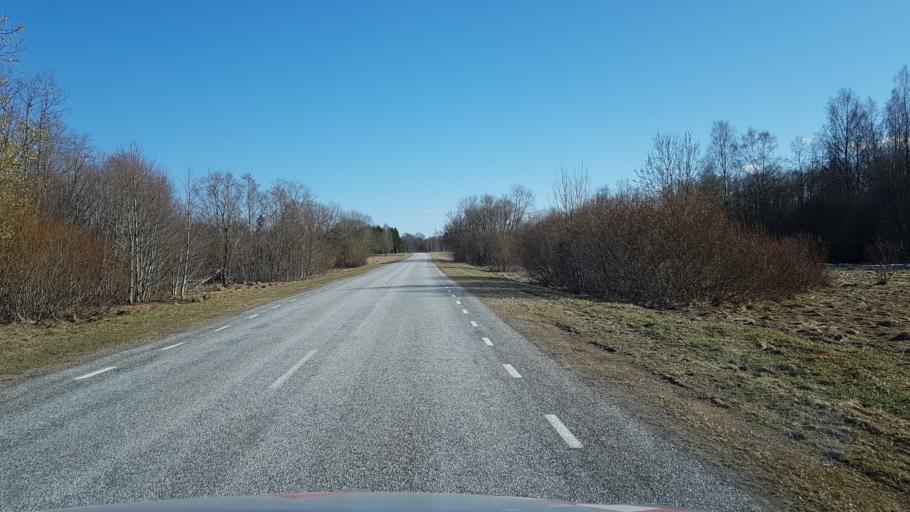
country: EE
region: Laeaene-Virumaa
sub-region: Haljala vald
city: Haljala
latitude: 59.4833
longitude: 26.1533
